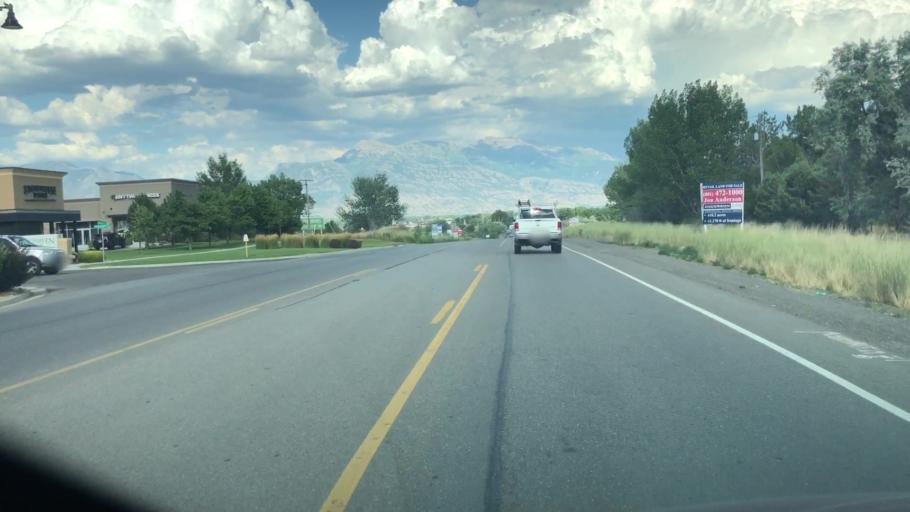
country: US
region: Utah
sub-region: Utah County
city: Saratoga Springs
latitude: 40.3874
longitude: -111.9100
